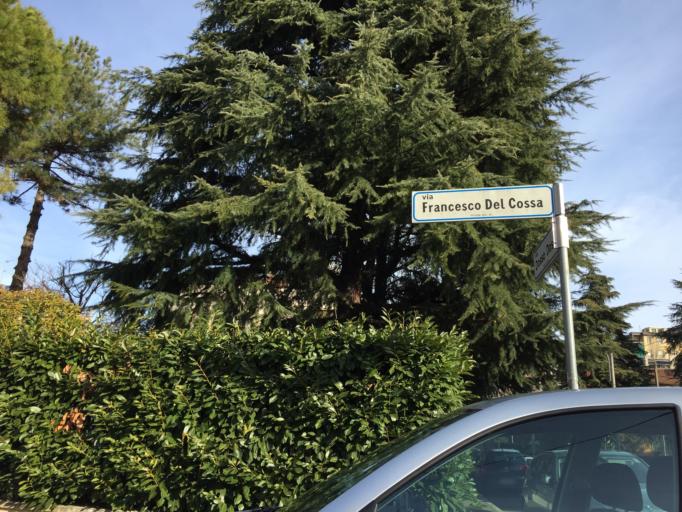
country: IT
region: Emilia-Romagna
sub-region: Provincia di Bologna
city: Casalecchio di Reno
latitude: 44.5014
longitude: 11.2988
